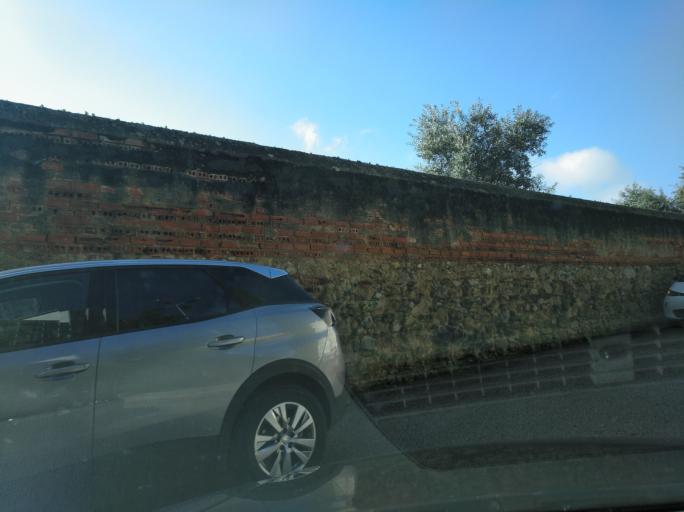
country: PT
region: Lisbon
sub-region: Odivelas
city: Pontinha
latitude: 38.7588
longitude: -9.1754
